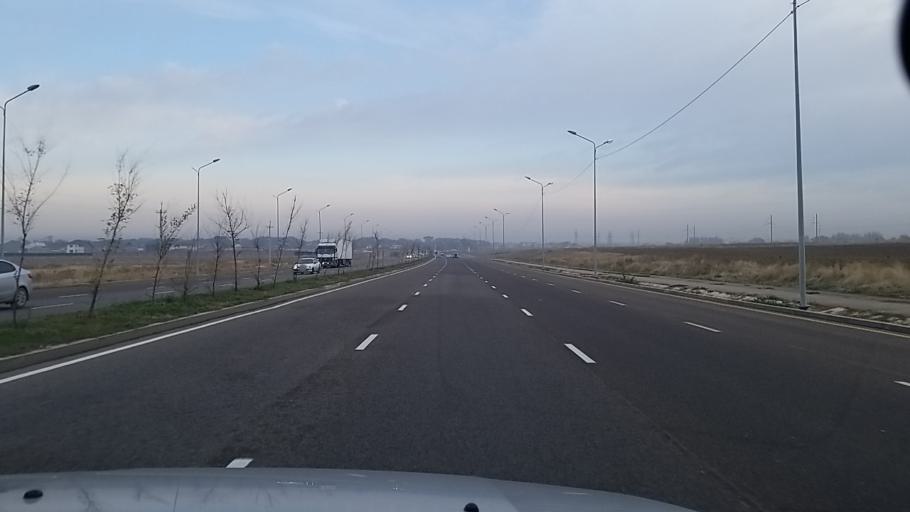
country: KZ
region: Almaty Oblysy
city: Burunday
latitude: 43.3437
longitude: 76.8339
